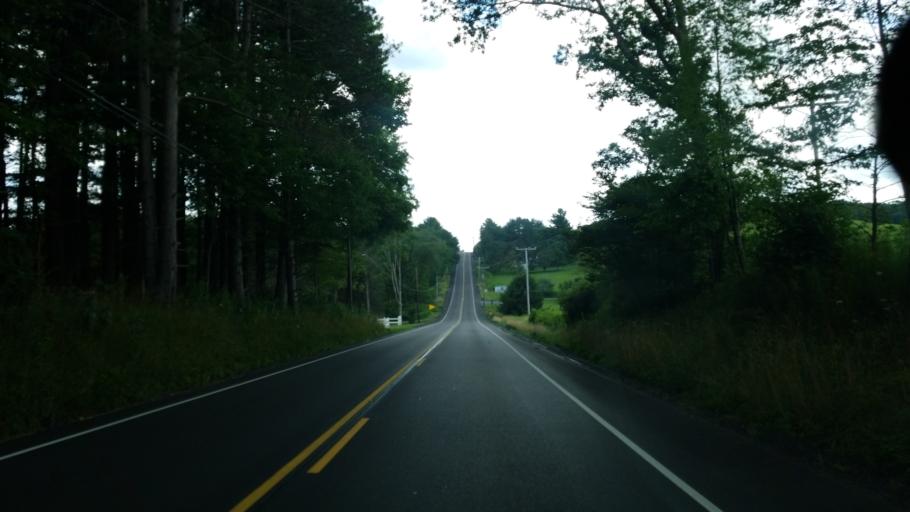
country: US
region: Pennsylvania
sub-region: Jefferson County
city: Brookville
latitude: 41.2461
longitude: -79.1108
